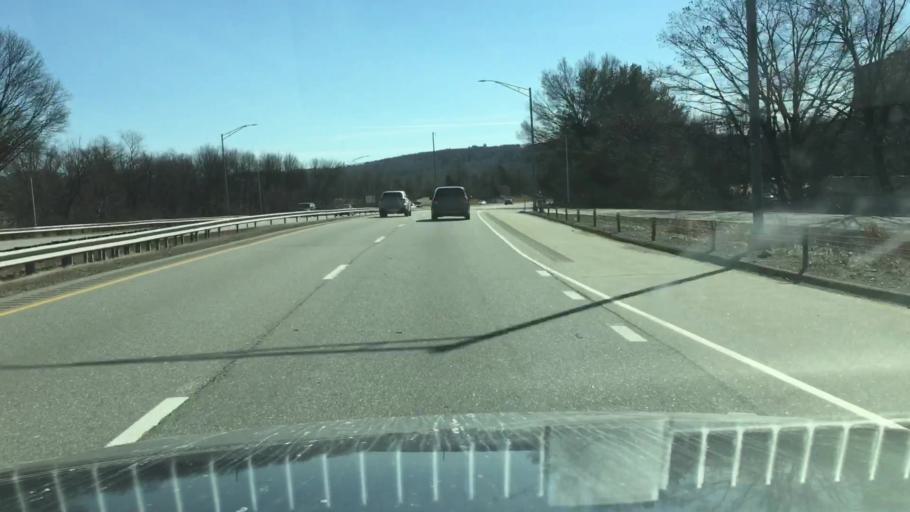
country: US
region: Connecticut
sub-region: New London County
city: Norwich
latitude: 41.5088
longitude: -72.1160
